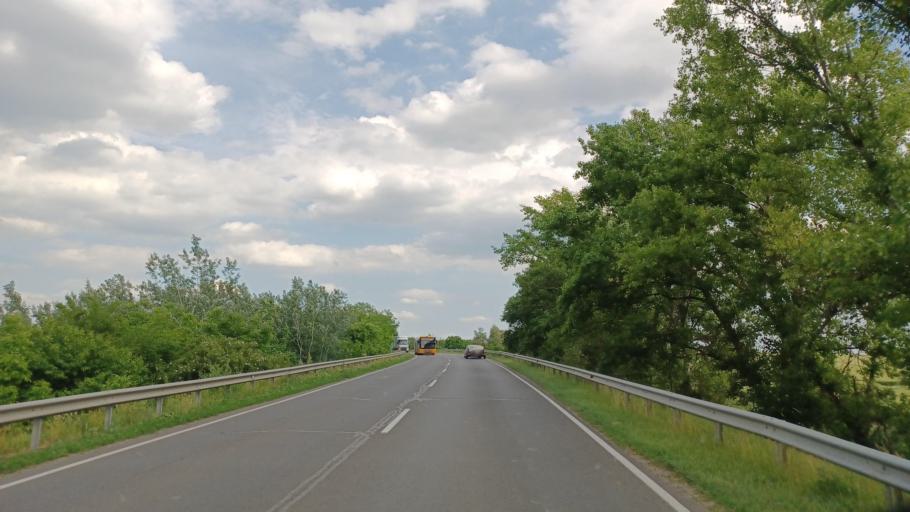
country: HU
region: Fejer
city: Eloszallas
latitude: 46.8218
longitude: 18.8715
